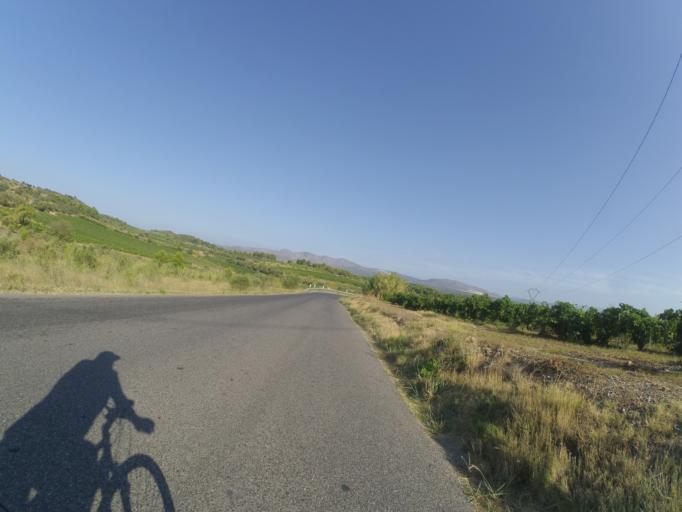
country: FR
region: Languedoc-Roussillon
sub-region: Departement des Pyrenees-Orientales
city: Baixas
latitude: 42.7673
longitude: 2.8263
